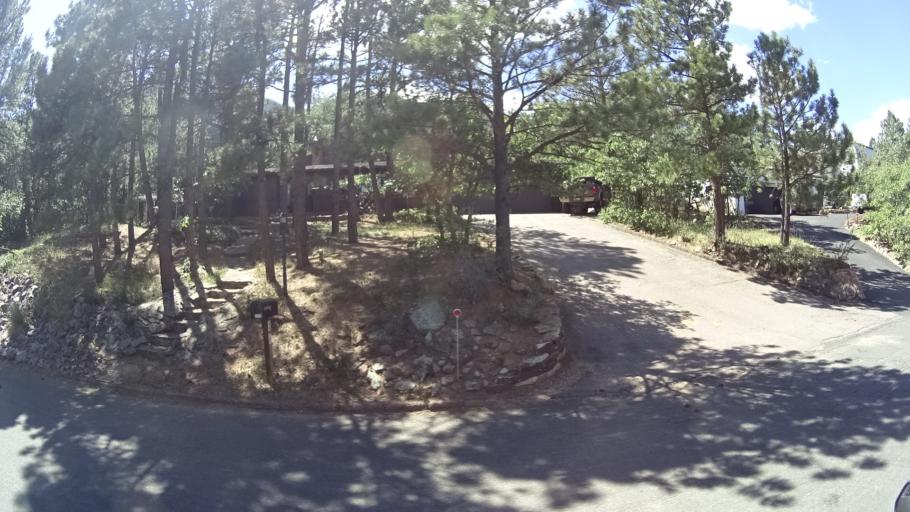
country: US
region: Colorado
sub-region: El Paso County
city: Colorado Springs
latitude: 38.7808
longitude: -104.8612
